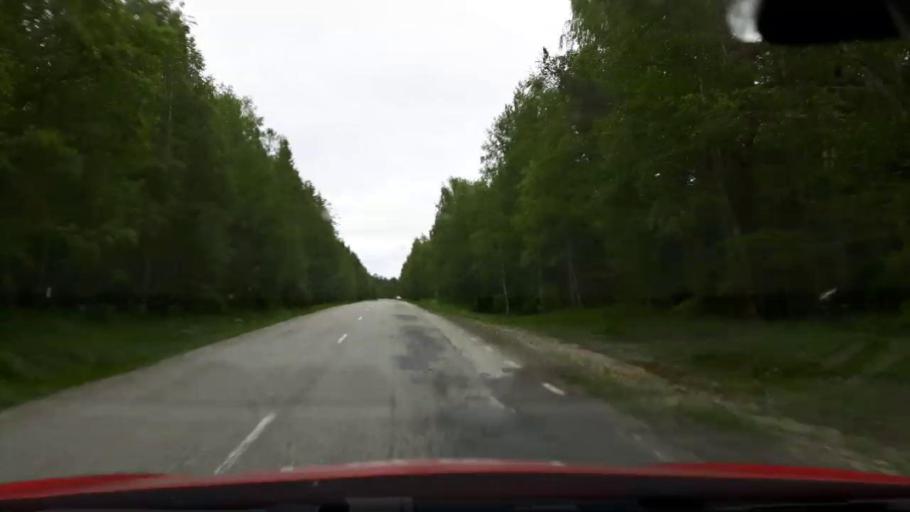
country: SE
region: Jaemtland
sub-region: Ragunda Kommun
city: Hammarstrand
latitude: 63.2356
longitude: 15.9196
